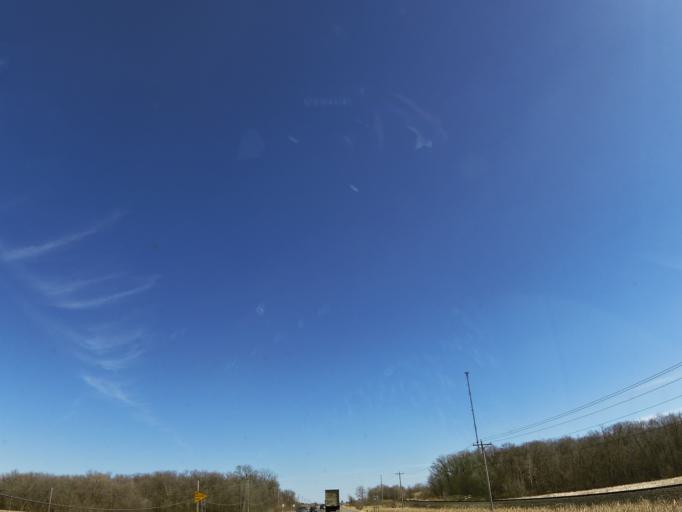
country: US
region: Minnesota
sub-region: Hennepin County
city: Medina
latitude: 45.0547
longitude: -93.5764
